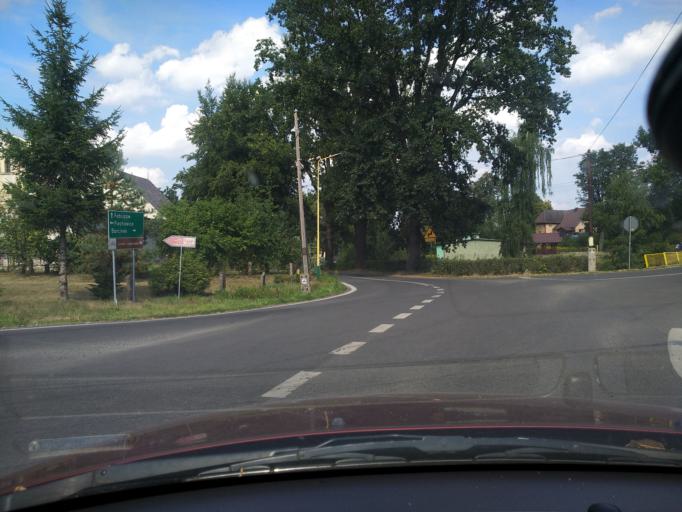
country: PL
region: Lower Silesian Voivodeship
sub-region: Powiat jeleniogorski
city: Stara Kamienica
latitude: 50.9156
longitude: 15.5728
